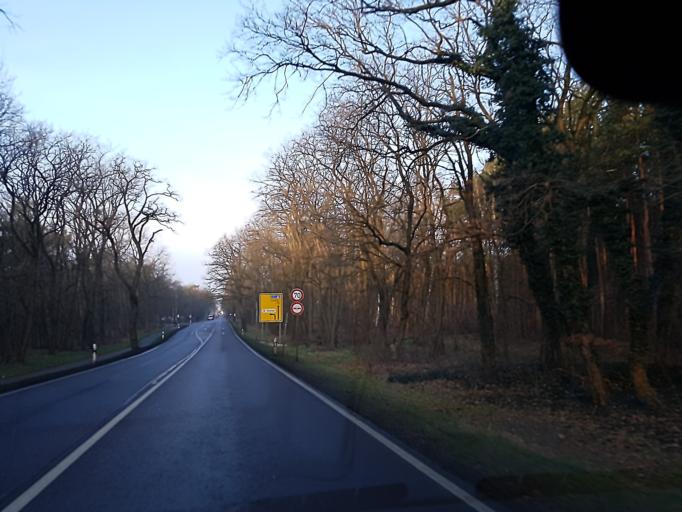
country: DE
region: Saxony-Anhalt
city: Coswig
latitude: 51.8807
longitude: 12.4805
